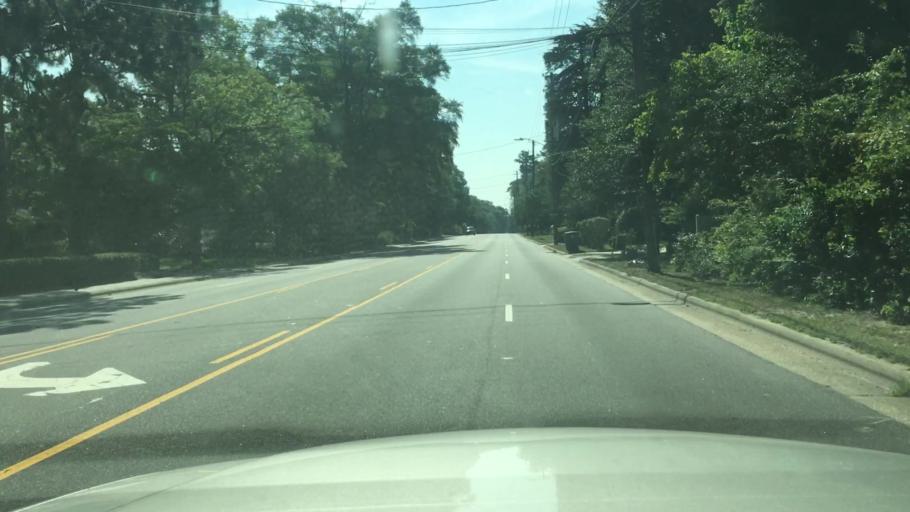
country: US
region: North Carolina
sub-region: Cumberland County
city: Fayetteville
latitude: 35.0601
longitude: -78.9133
